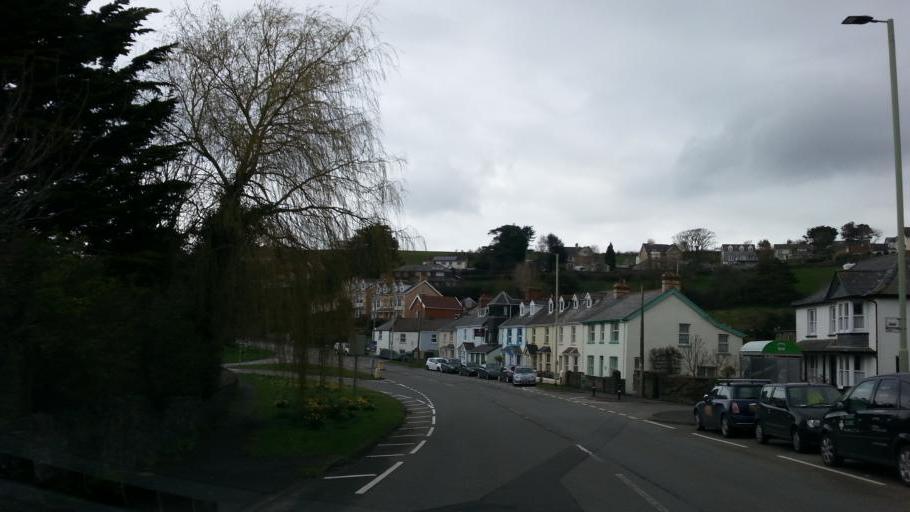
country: GB
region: England
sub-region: Devon
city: Appledore
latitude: 51.0487
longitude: -4.1783
